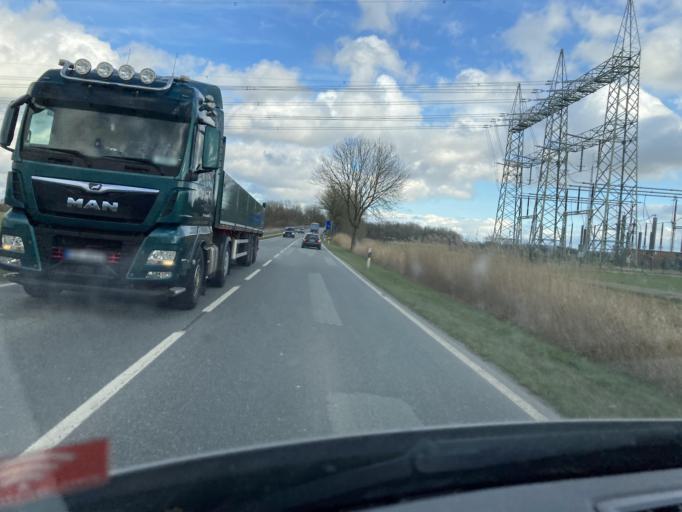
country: DE
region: Lower Saxony
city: Sande
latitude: 53.4854
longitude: 7.9970
